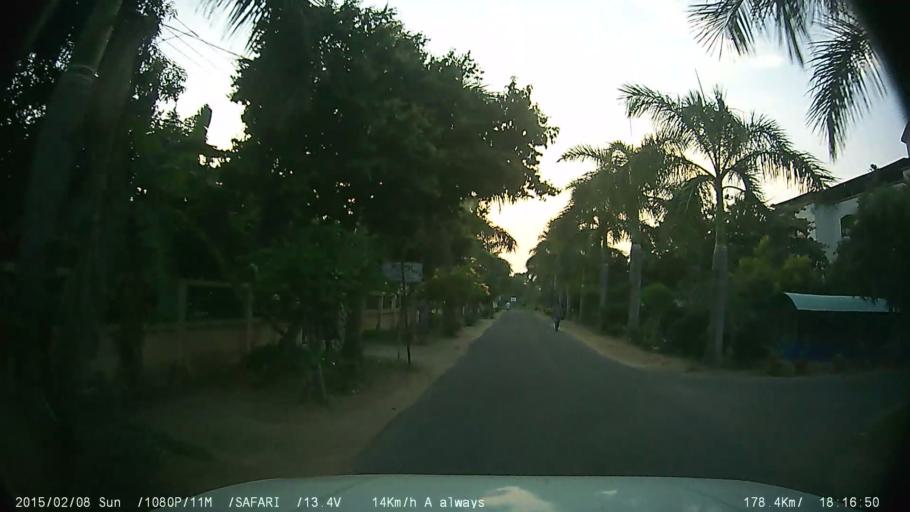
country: IN
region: Kerala
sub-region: Palakkad district
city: Palakkad
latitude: 10.7379
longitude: 76.6514
